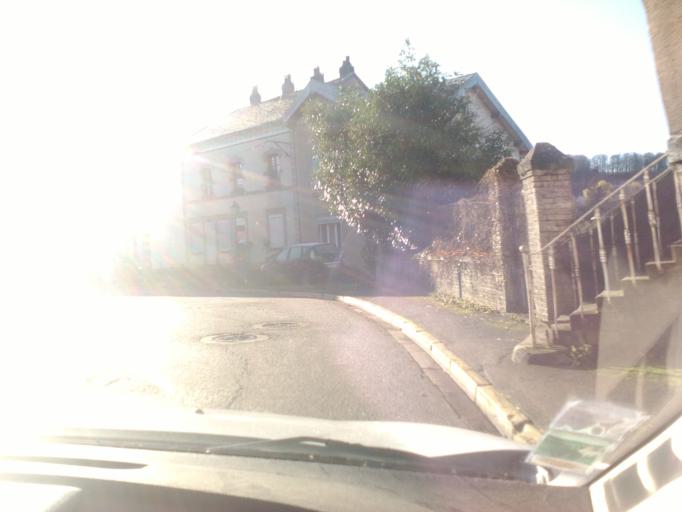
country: FR
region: Lorraine
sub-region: Departement des Vosges
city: Xertigny
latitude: 48.0463
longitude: 6.4016
